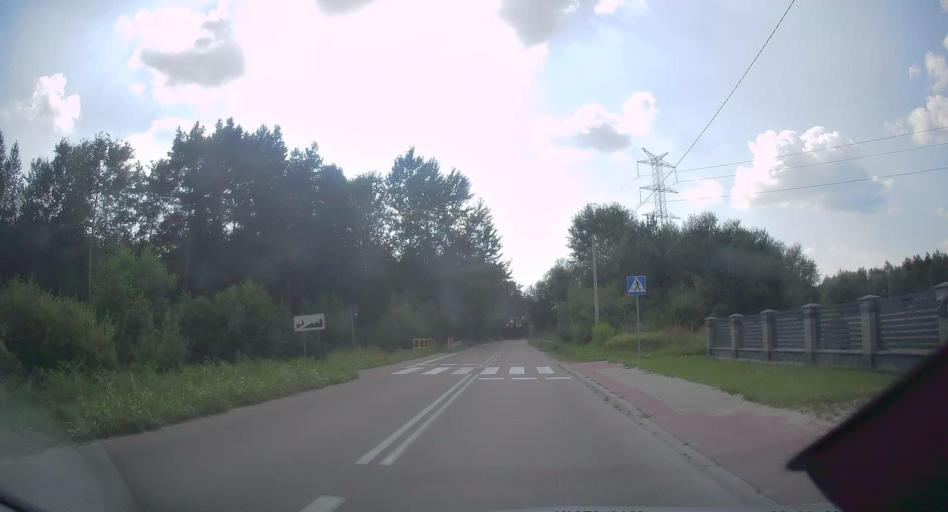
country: PL
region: Swietokrzyskie
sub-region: Powiat jedrzejowski
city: Malogoszcz
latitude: 50.8660
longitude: 20.3074
